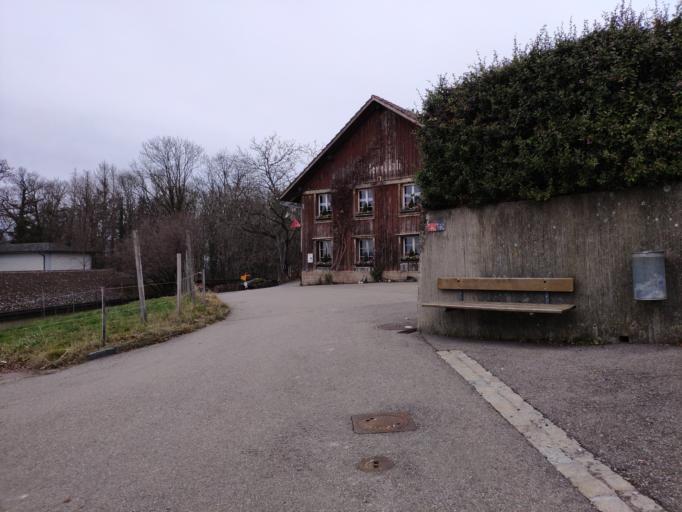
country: CH
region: Basel-City
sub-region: Basel-Stadt
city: Bettingen
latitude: 47.5728
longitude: 7.6795
